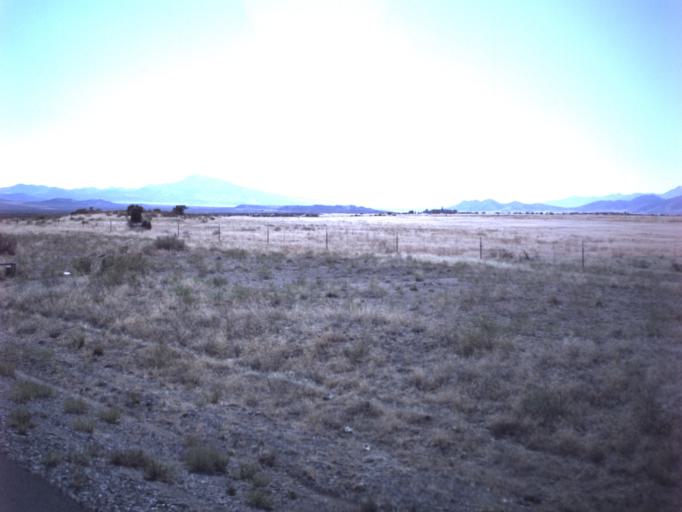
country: US
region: Utah
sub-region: Tooele County
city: Grantsville
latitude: 40.2489
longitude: -112.7283
